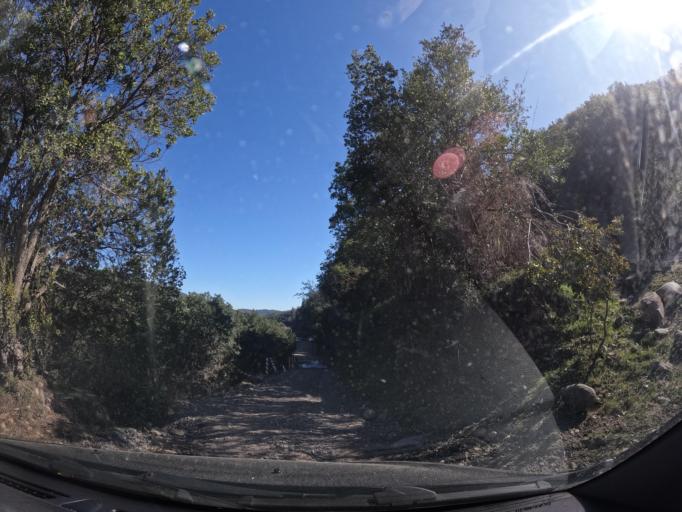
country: CL
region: Maule
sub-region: Provincia de Linares
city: Longavi
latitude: -36.2295
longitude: -71.4004
